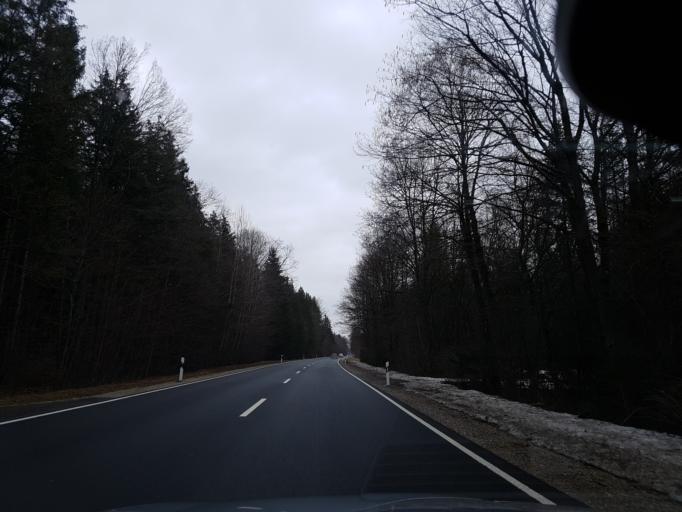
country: DE
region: Bavaria
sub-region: Upper Bavaria
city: Hohenkirchen-Siegertsbrunn
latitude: 47.9825
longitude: 11.7306
